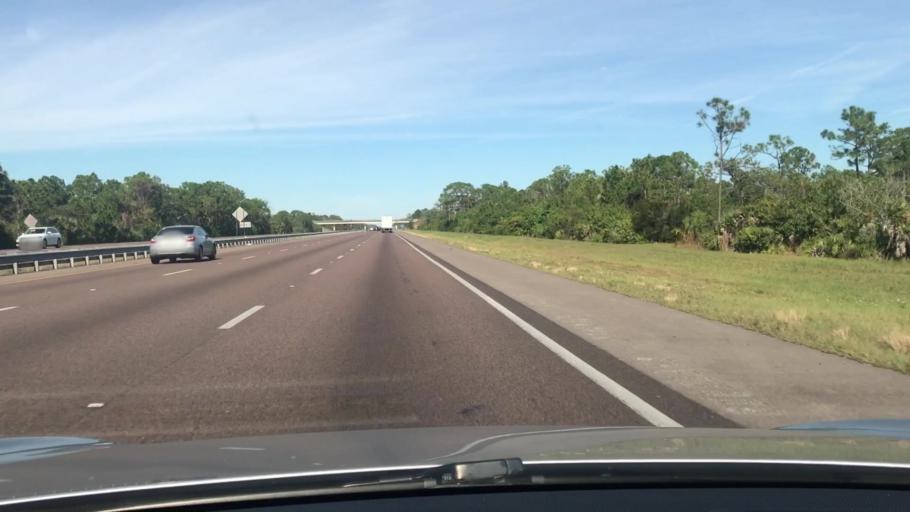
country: US
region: Florida
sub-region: Brevard County
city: Grant-Valkaria
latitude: 27.9191
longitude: -80.6007
